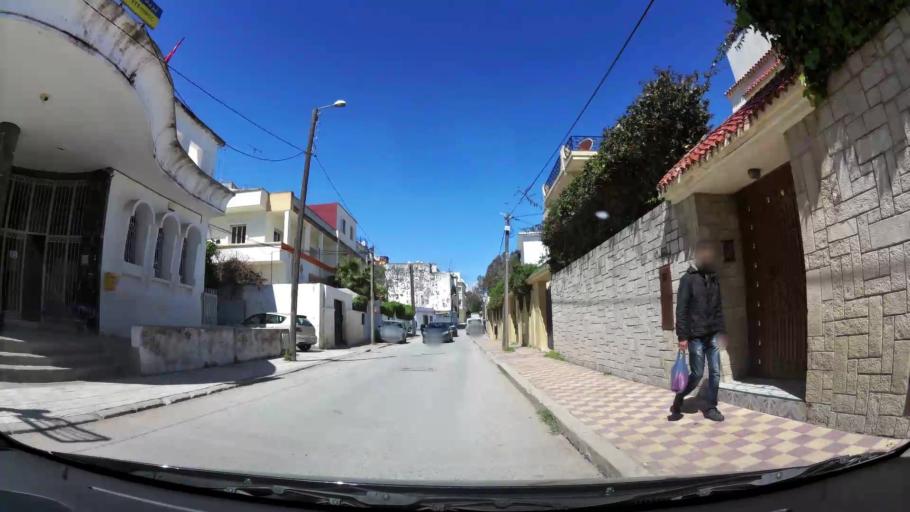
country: MA
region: Tanger-Tetouan
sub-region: Tanger-Assilah
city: Tangier
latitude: 35.7773
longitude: -5.8308
